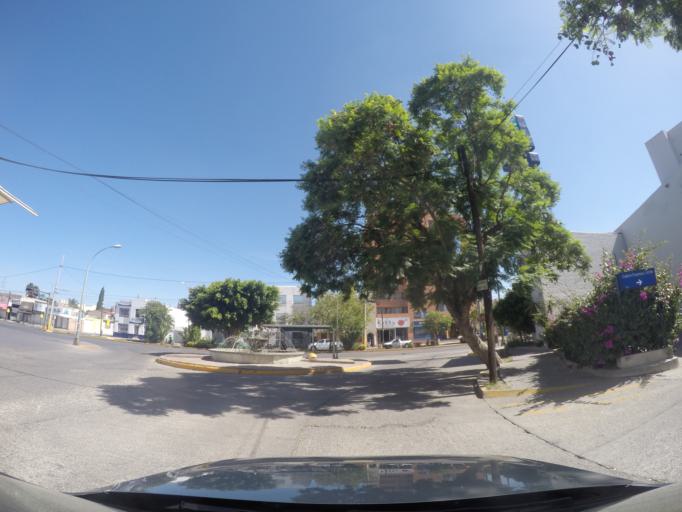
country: MX
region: San Luis Potosi
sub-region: San Luis Potosi
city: San Luis Potosi
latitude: 22.1490
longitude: -101.0114
